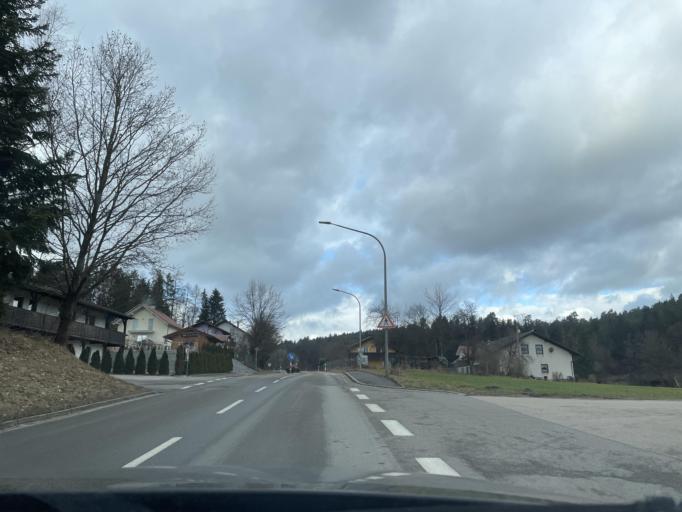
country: DE
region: Bavaria
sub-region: Upper Palatinate
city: Blaibach
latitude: 49.1704
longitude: 12.8044
